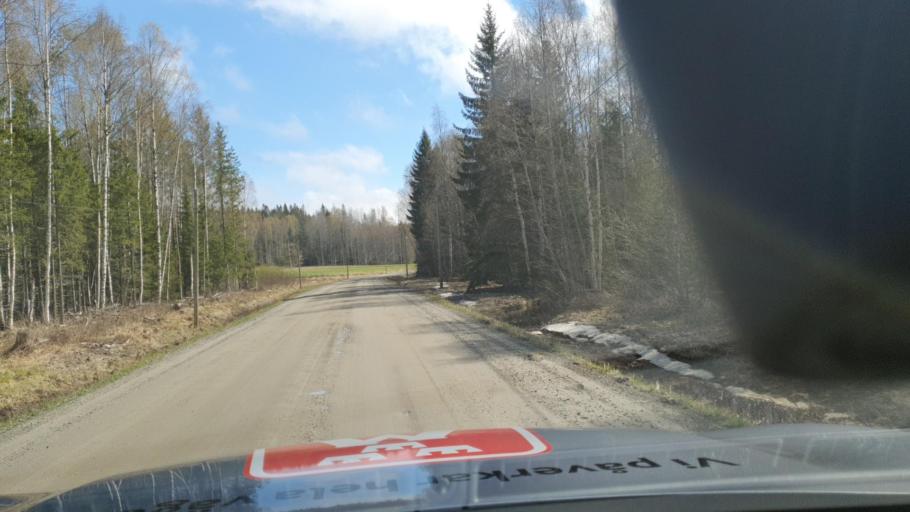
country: SE
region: Vaesterbotten
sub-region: Bjurholms Kommun
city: Bjurholm
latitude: 63.6952
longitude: 18.9550
